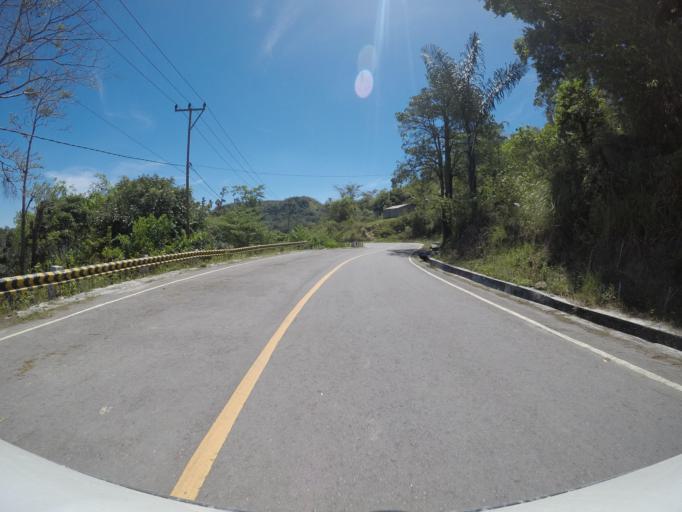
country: TL
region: Manatuto
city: Manatuto
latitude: -8.7980
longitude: 125.9701
